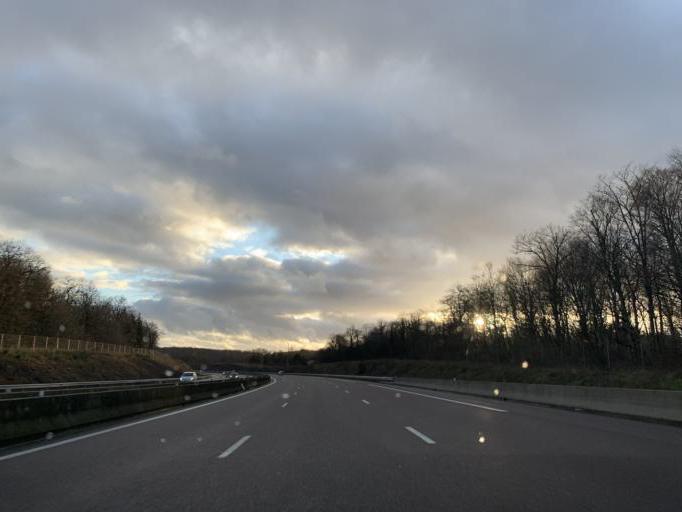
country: FR
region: Champagne-Ardenne
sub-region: Departement de la Haute-Marne
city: Langres
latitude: 47.7656
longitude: 5.1895
